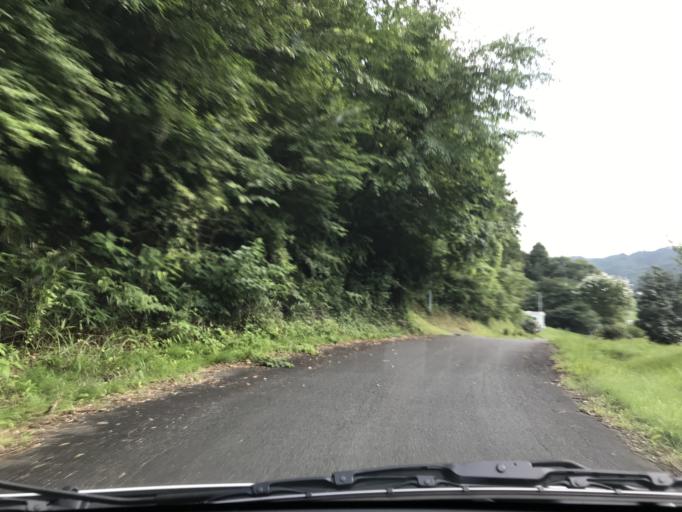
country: JP
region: Iwate
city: Mizusawa
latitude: 39.0279
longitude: 141.0872
